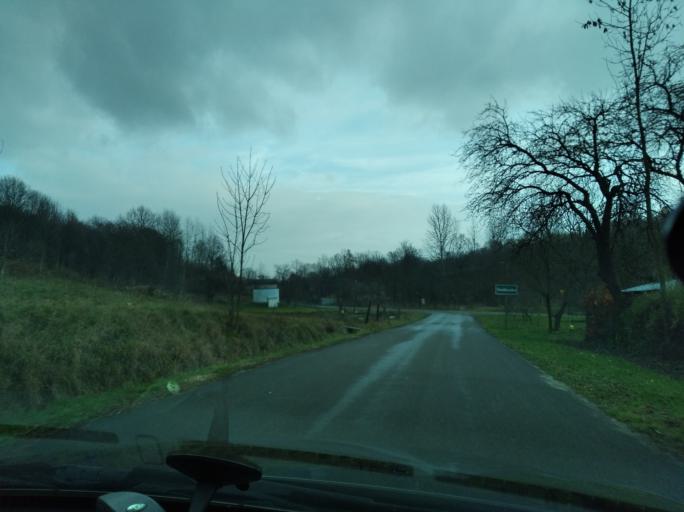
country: PL
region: Subcarpathian Voivodeship
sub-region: Powiat przeworski
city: Sietesz
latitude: 49.9667
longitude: 22.3454
